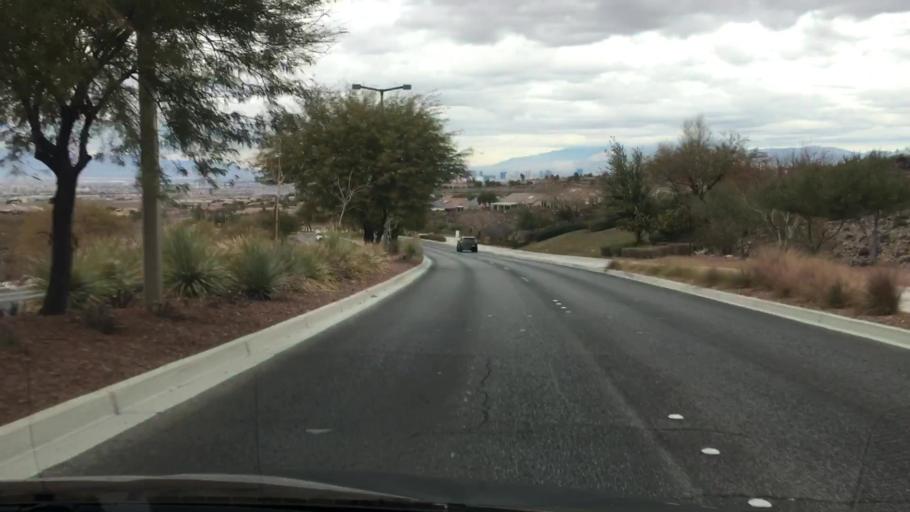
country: US
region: Nevada
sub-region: Clark County
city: Whitney
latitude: 35.9550
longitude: -115.1145
